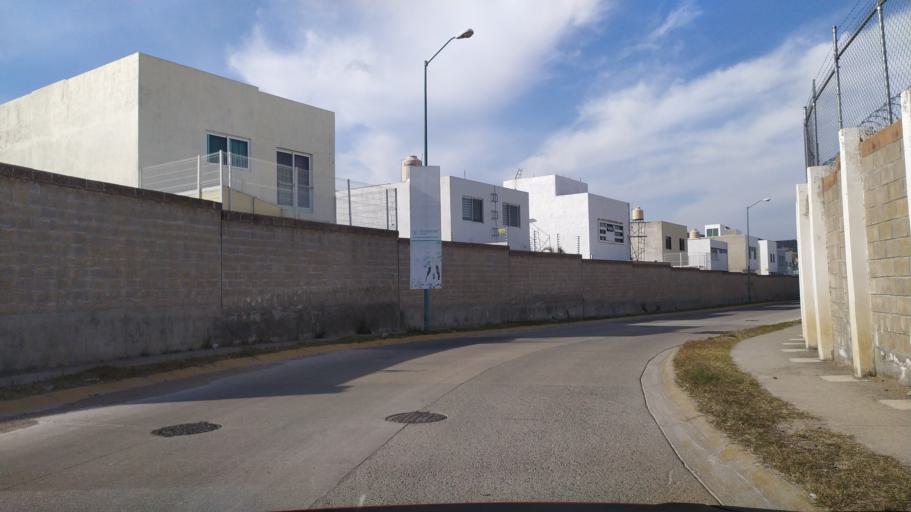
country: MX
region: Jalisco
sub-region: Tlajomulco de Zuniga
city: Palomar
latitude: 20.6279
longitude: -103.4824
